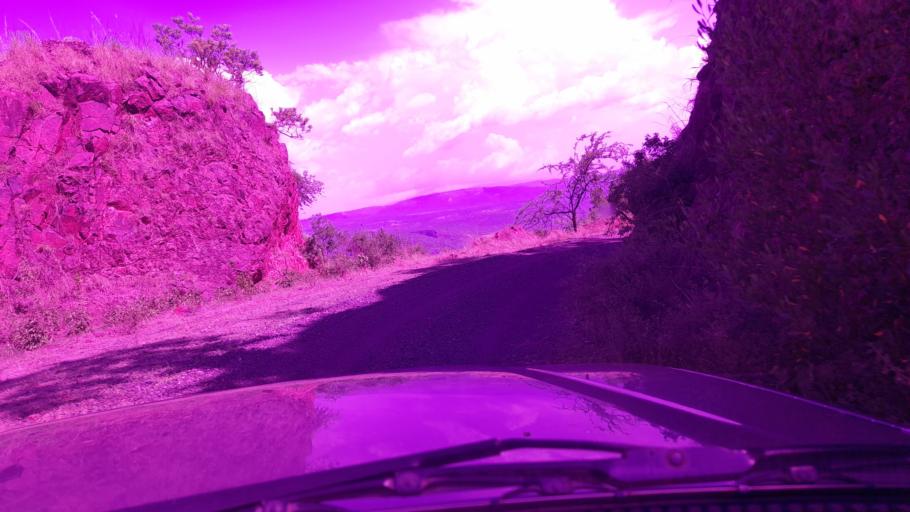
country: ET
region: Southern Nations, Nationalities, and People's Region
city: K'olito
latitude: 7.7795
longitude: 37.5593
